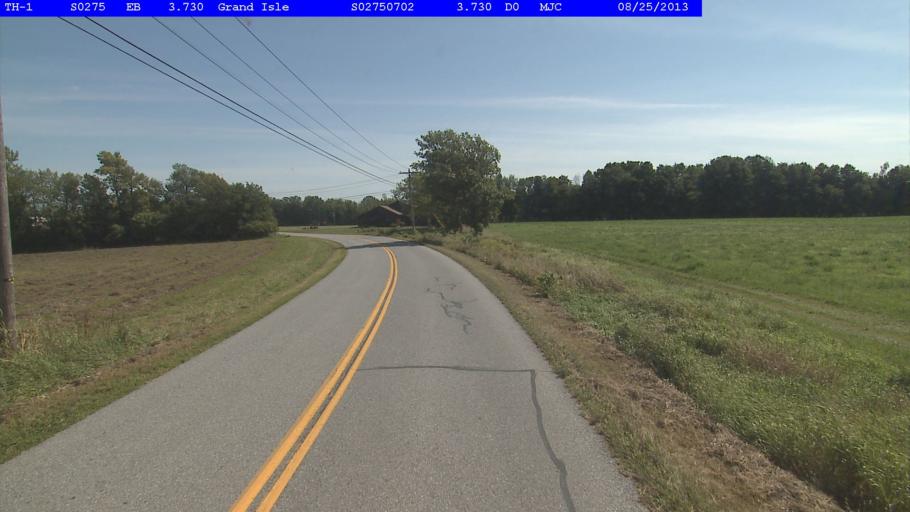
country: US
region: Vermont
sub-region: Grand Isle County
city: North Hero
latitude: 44.7360
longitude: -73.3063
